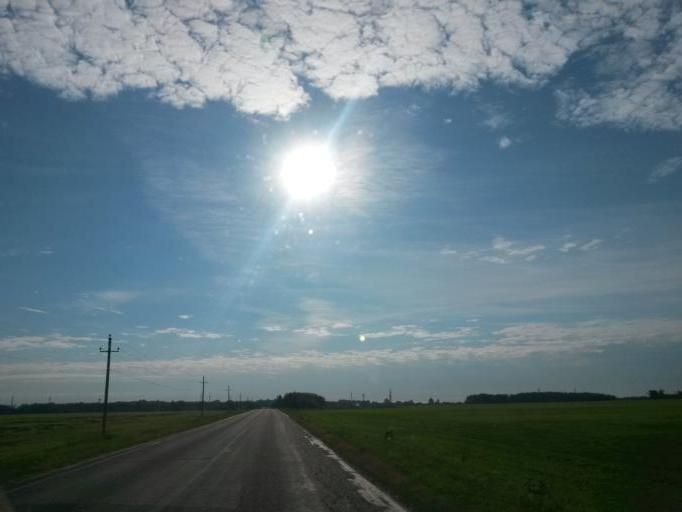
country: RU
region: Moskovskaya
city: Belyye Stolby
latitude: 55.2697
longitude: 37.8101
